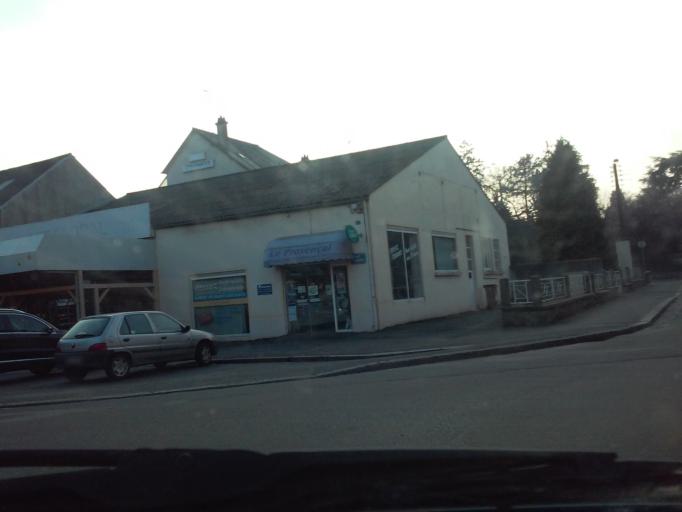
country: FR
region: Brittany
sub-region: Departement d'Ille-et-Vilaine
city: Fougeres
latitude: 48.3481
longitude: -1.1948
